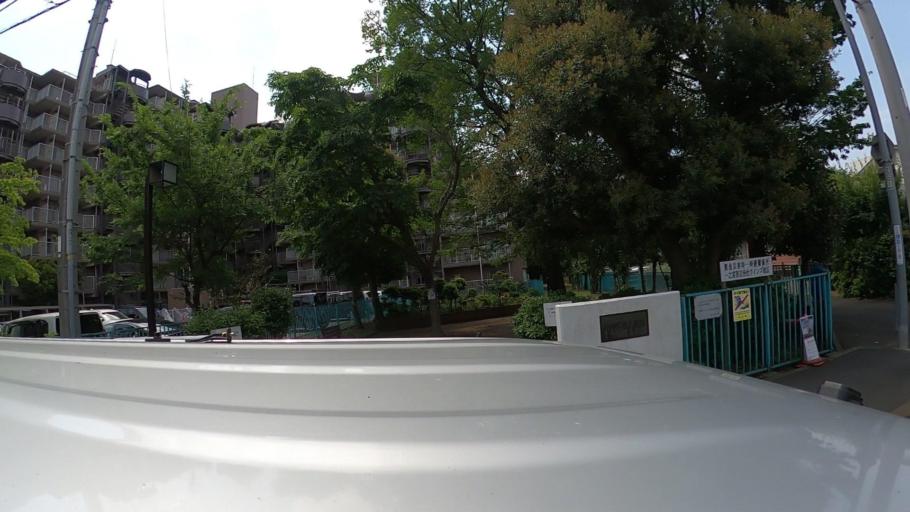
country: JP
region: Kanagawa
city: Chigasaki
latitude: 35.3646
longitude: 139.3783
